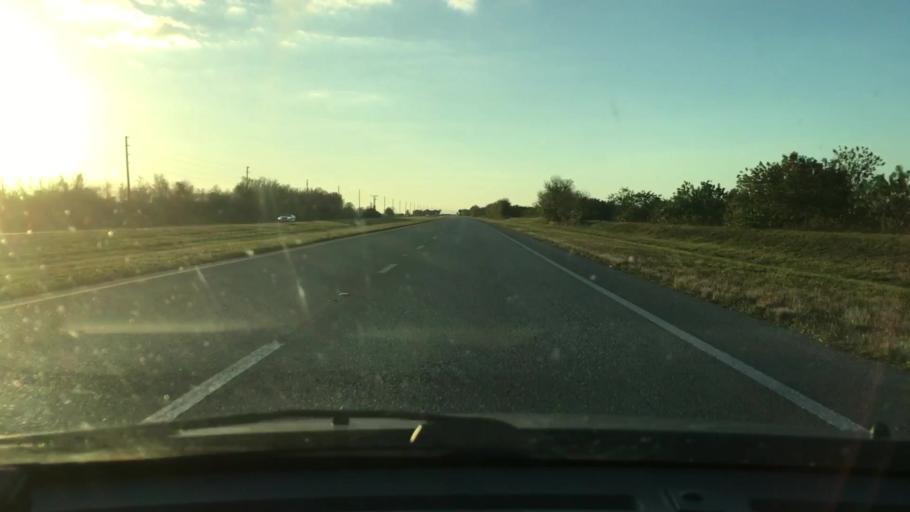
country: US
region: Florida
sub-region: Indian River County
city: Fellsmere
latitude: 27.6409
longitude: -80.6639
